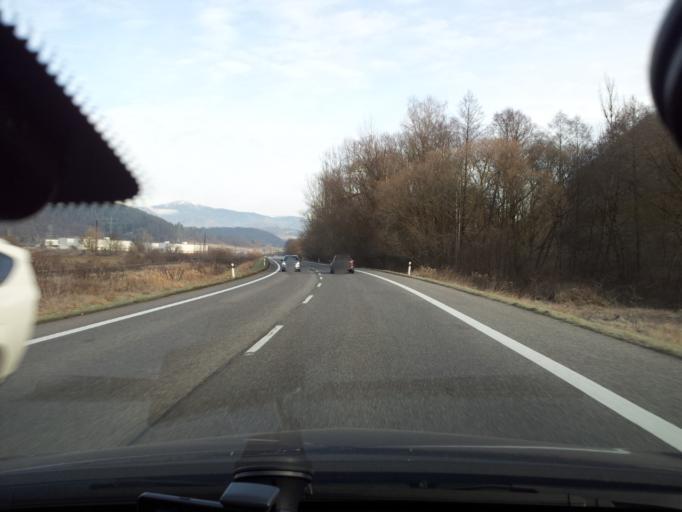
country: SK
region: Banskobystricky
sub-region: Okres Banska Bystrica
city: Banska Bystrica
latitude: 48.7480
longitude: 19.2526
